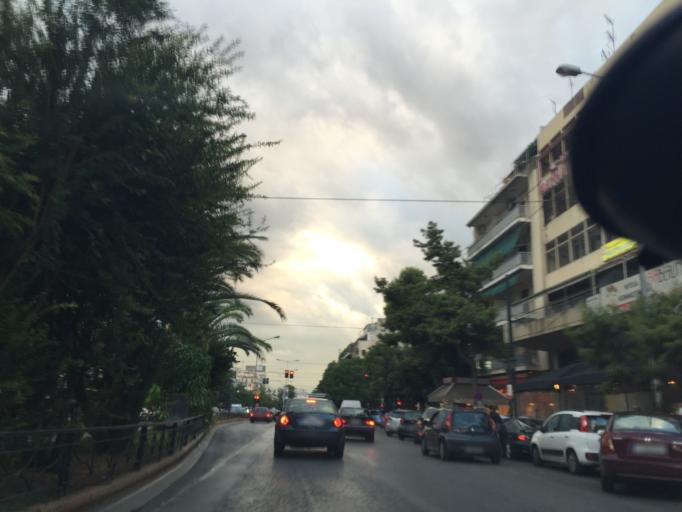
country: GR
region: Attica
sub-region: Nomarchia Athinas
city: Kallithea
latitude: 37.9566
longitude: 23.7028
